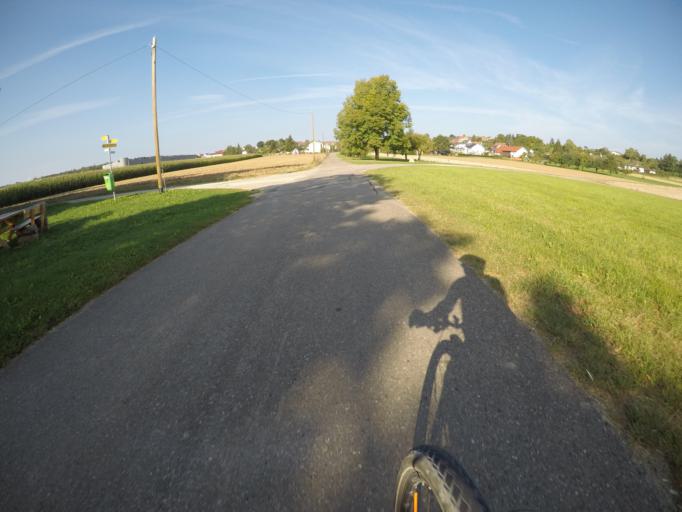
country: DE
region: Baden-Wuerttemberg
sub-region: Tuebingen Region
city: Ballendorf
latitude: 48.6044
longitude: 10.0773
